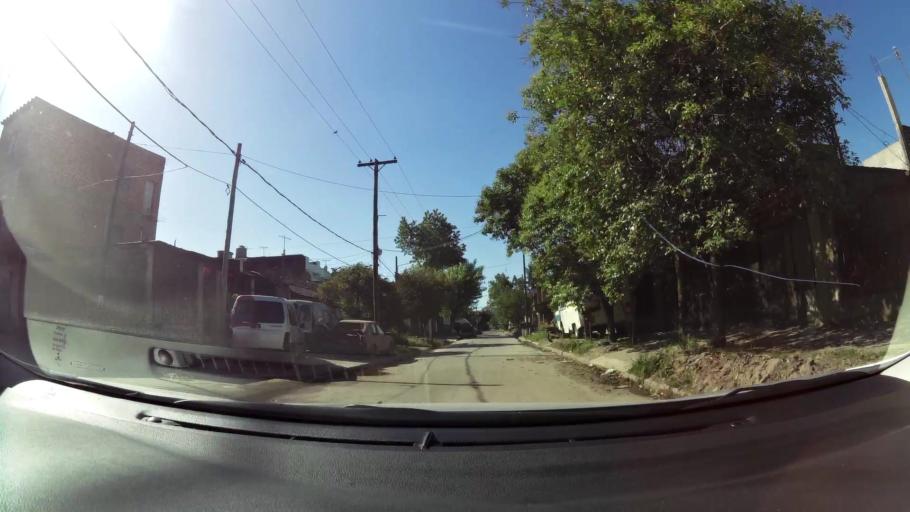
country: AR
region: Buenos Aires F.D.
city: Villa Lugano
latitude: -34.7067
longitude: -58.4762
